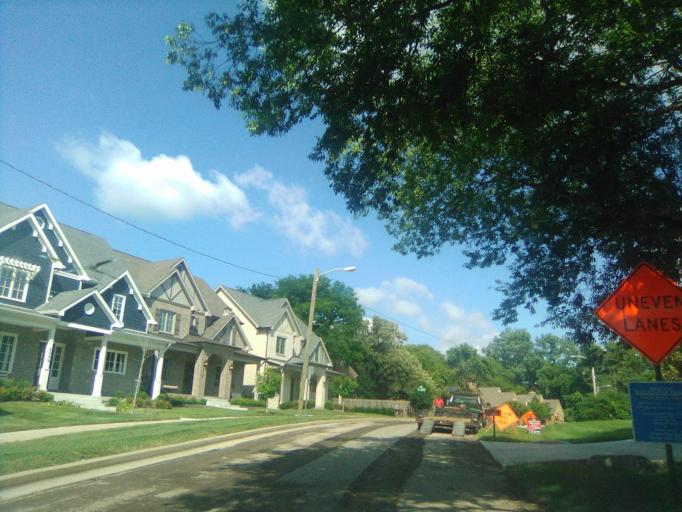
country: US
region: Tennessee
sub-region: Davidson County
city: Belle Meade
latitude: 36.1043
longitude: -86.8704
